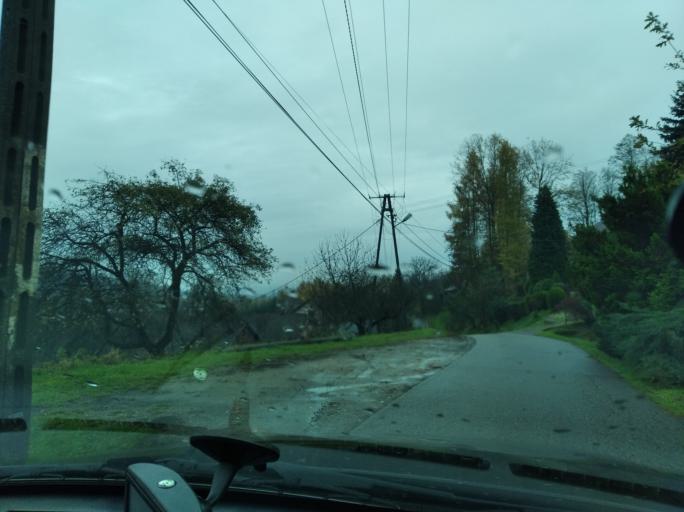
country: PL
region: Subcarpathian Voivodeship
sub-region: Powiat strzyzowski
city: Babica
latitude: 49.9316
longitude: 21.8881
